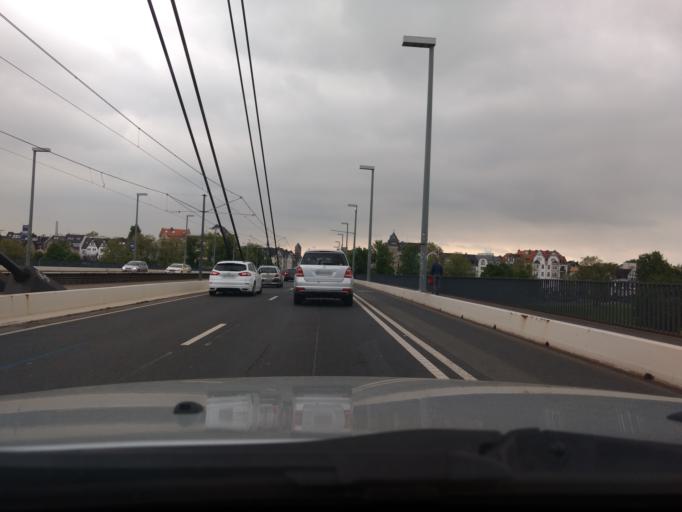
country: DE
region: North Rhine-Westphalia
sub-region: Regierungsbezirk Dusseldorf
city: Dusseldorf
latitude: 51.2317
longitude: 6.7661
